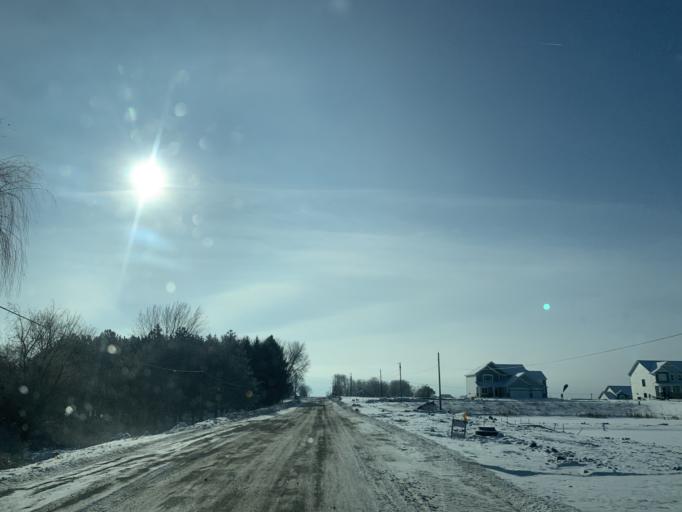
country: US
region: Minnesota
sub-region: Dakota County
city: Lakeville
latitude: 44.6588
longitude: -93.2275
